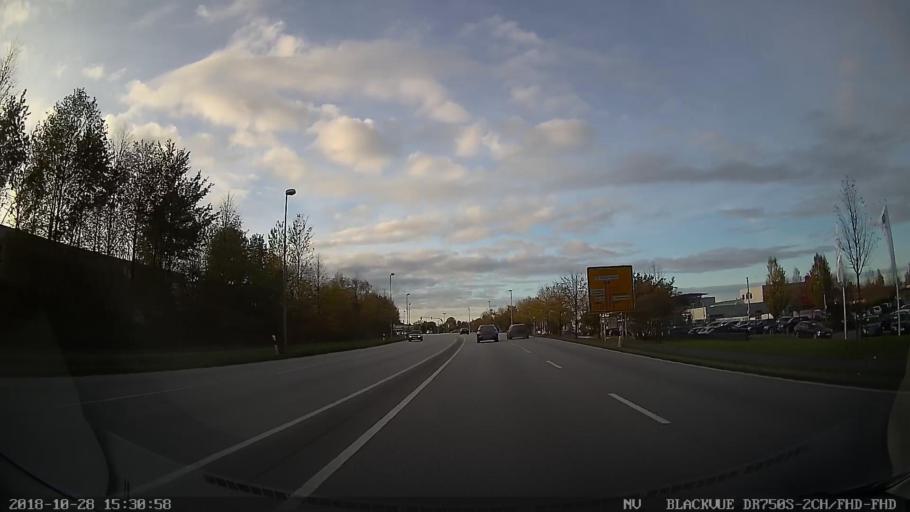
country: DE
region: Schleswig-Holstein
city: Kolln-Reisiek
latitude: 53.7462
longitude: 9.6993
